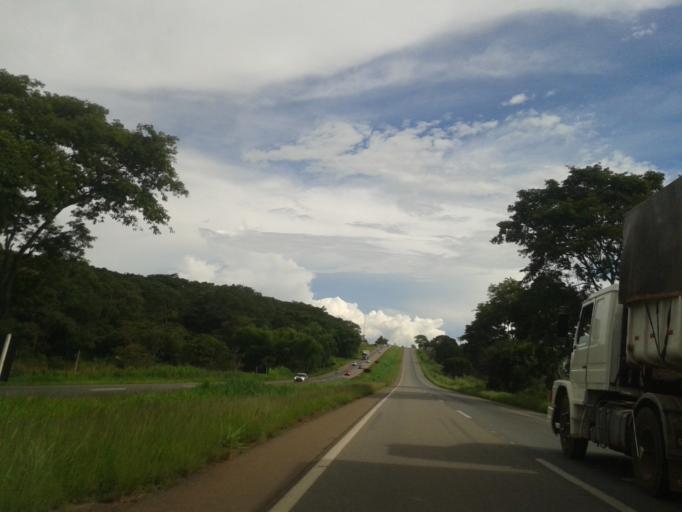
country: BR
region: Goias
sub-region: Hidrolandia
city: Hidrolandia
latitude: -16.9816
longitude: -49.2298
